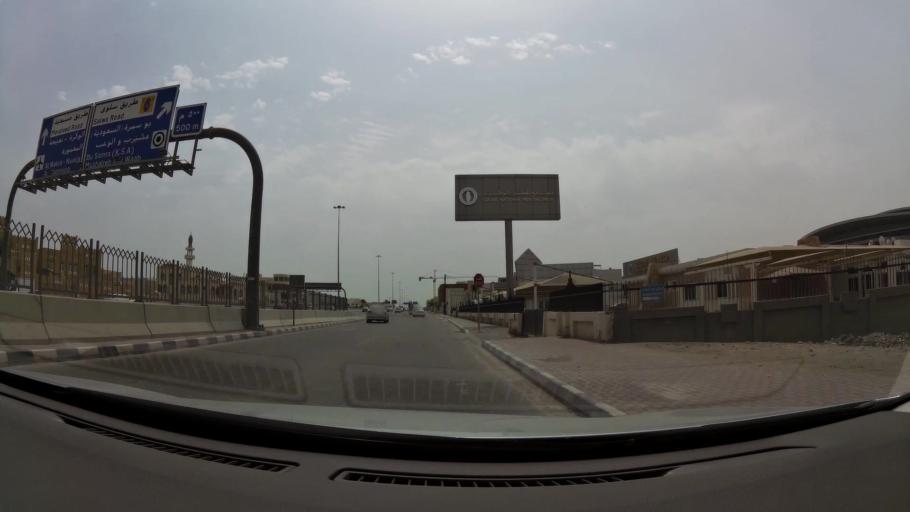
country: QA
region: Baladiyat ad Dawhah
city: Doha
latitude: 25.2720
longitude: 51.4913
